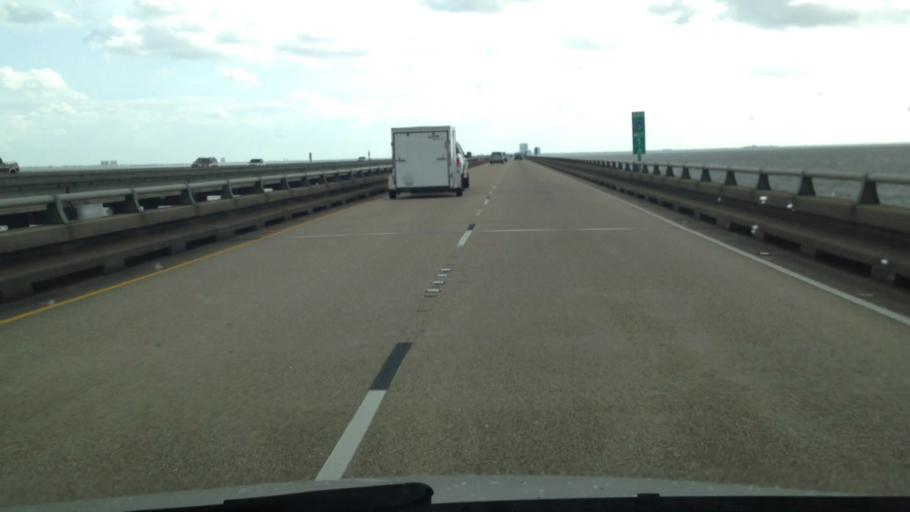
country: US
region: Louisiana
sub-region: Jefferson Parish
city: Metairie
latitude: 30.1022
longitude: -90.1399
